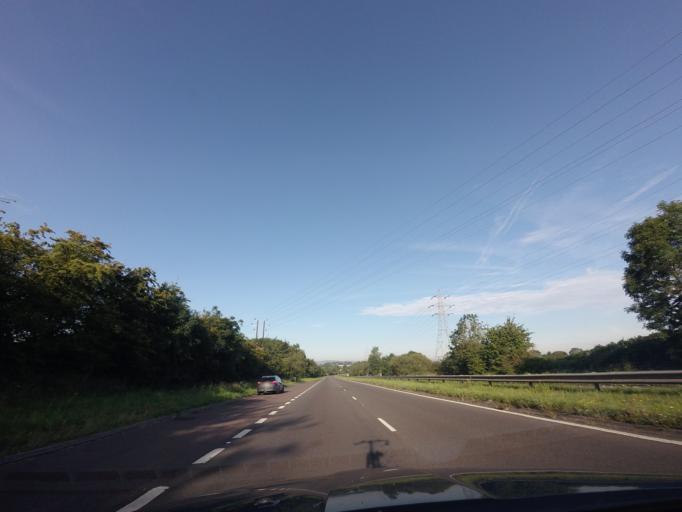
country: GB
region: England
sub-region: Derbyshire
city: Pilsley
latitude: 53.2007
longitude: -1.3513
